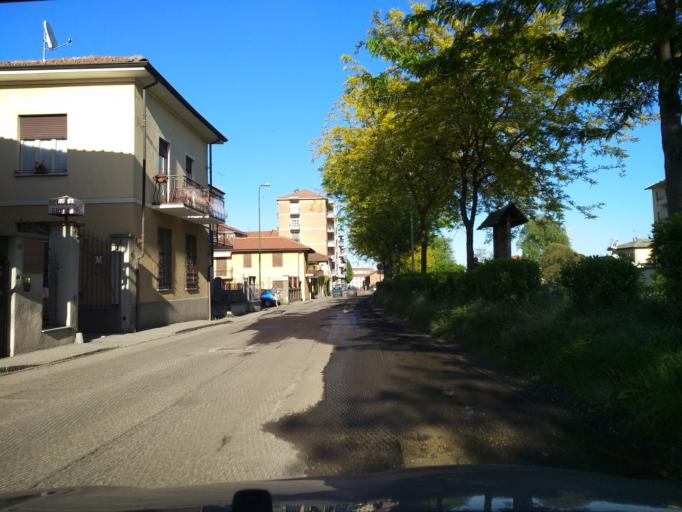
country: IT
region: Piedmont
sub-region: Provincia di Torino
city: Pinerolo
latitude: 44.8816
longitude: 7.3258
